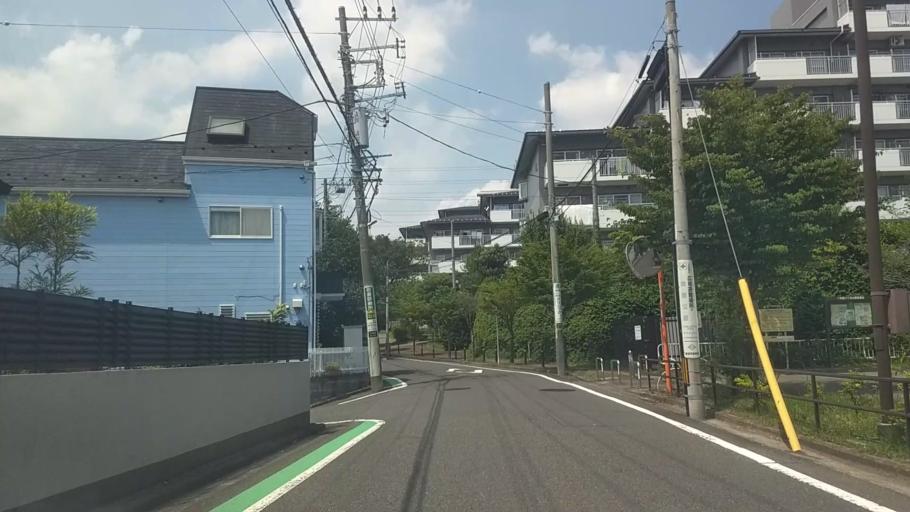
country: JP
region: Kanagawa
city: Yokohama
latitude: 35.4912
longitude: 139.6168
